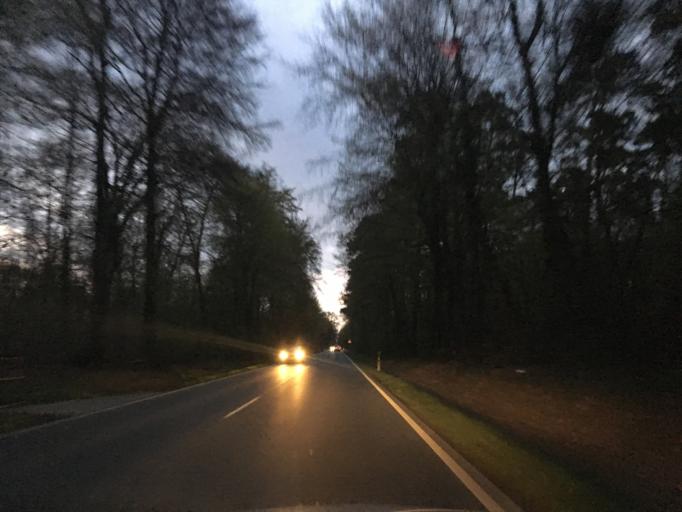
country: DE
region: Hesse
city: Morfelden-Walldorf
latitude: 49.9568
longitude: 8.5776
